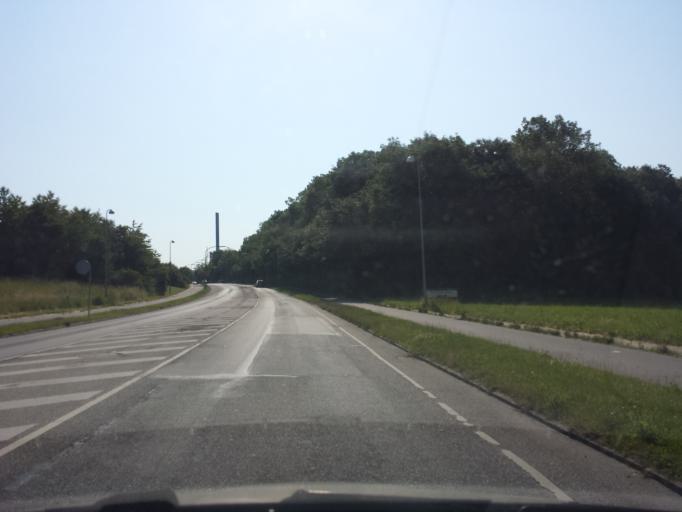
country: DK
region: Capital Region
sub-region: Ballerup Kommune
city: Malov
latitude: 55.7287
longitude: 12.3345
